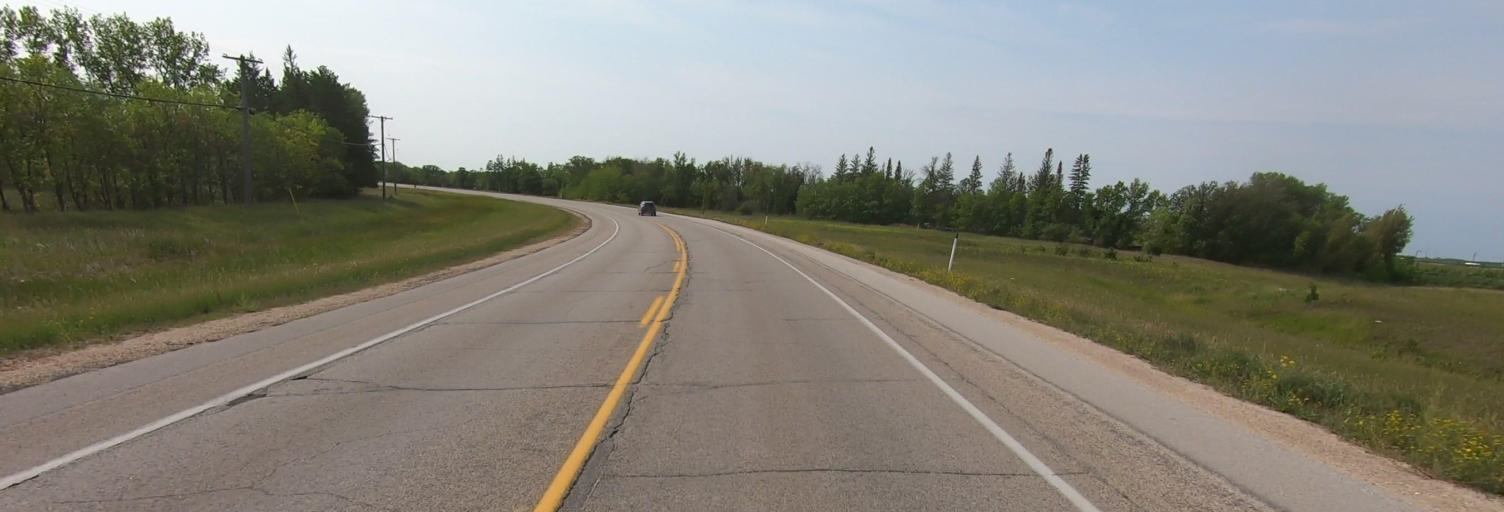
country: CA
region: Manitoba
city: Winnipeg
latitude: 49.7434
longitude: -97.1229
